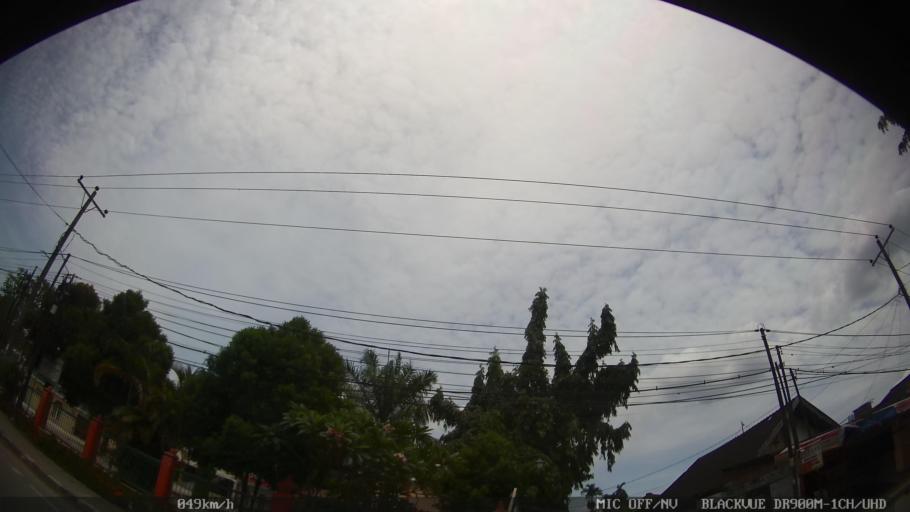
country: ID
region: North Sumatra
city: Deli Tua
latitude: 3.5345
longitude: 98.6487
